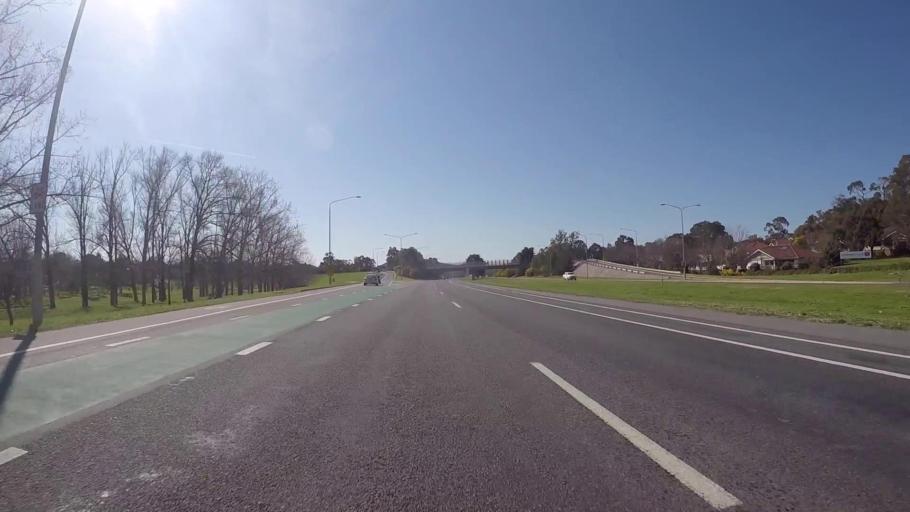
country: AU
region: Australian Capital Territory
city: Forrest
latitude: -35.3286
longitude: 149.0863
